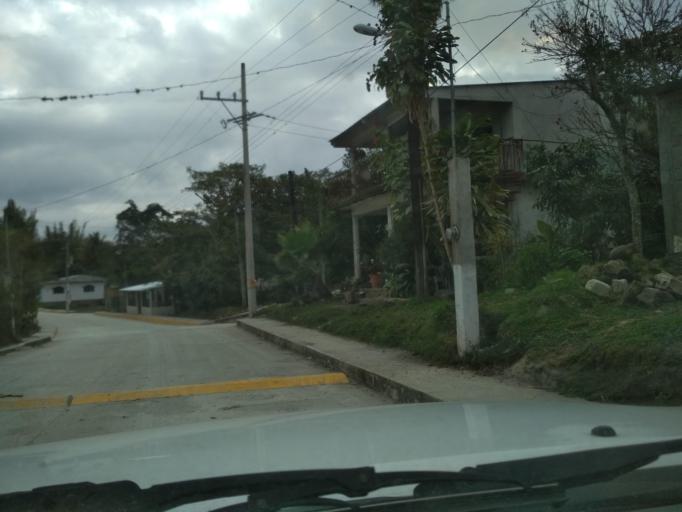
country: MX
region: Veracruz
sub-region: Coatepec
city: Tuzamapan
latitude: 19.3689
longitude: -96.8815
